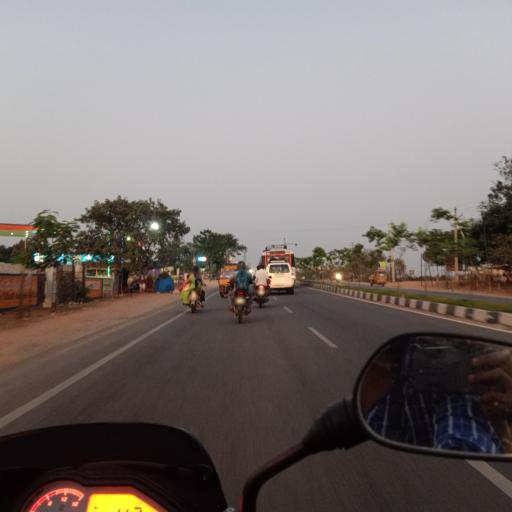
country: IN
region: Telangana
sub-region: Rangareddi
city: Secunderabad
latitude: 17.5591
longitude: 78.5437
